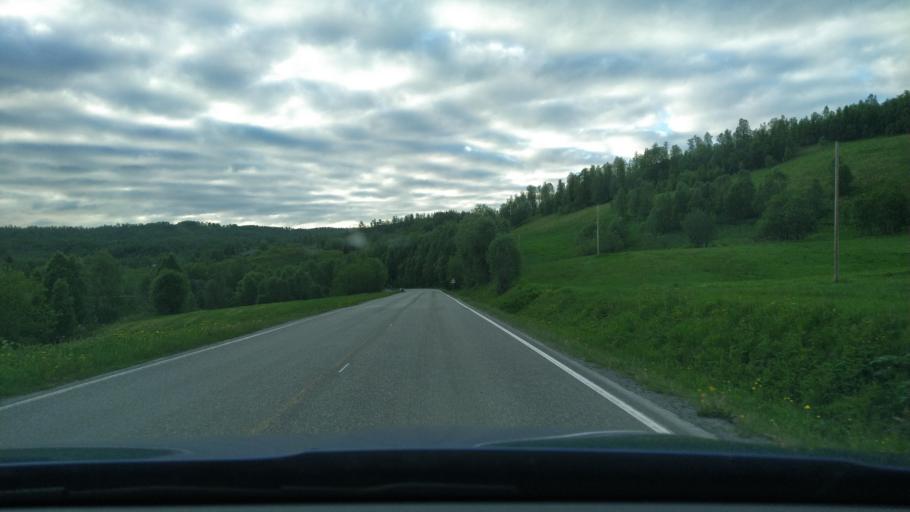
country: NO
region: Troms
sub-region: Sorreisa
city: Sorreisa
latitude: 69.0932
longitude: 18.3399
